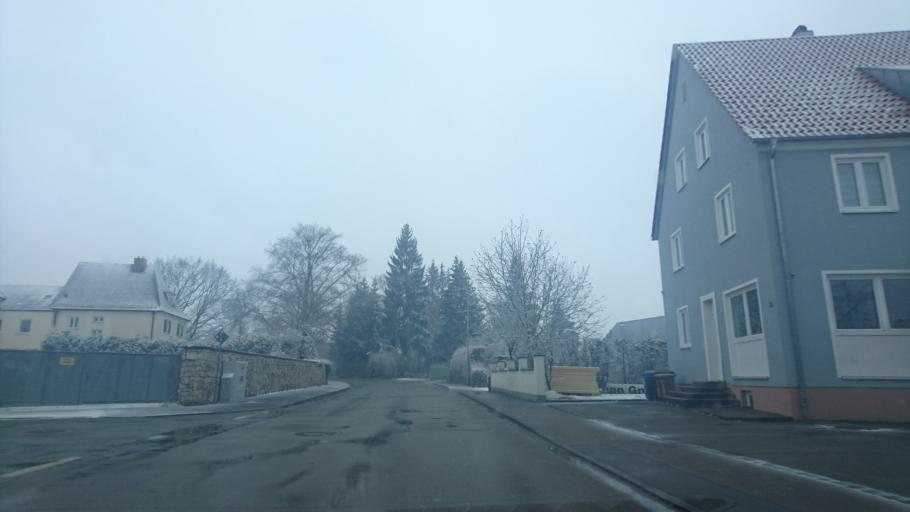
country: DE
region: Bavaria
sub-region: Swabia
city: Wertingen
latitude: 48.5577
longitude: 10.6838
